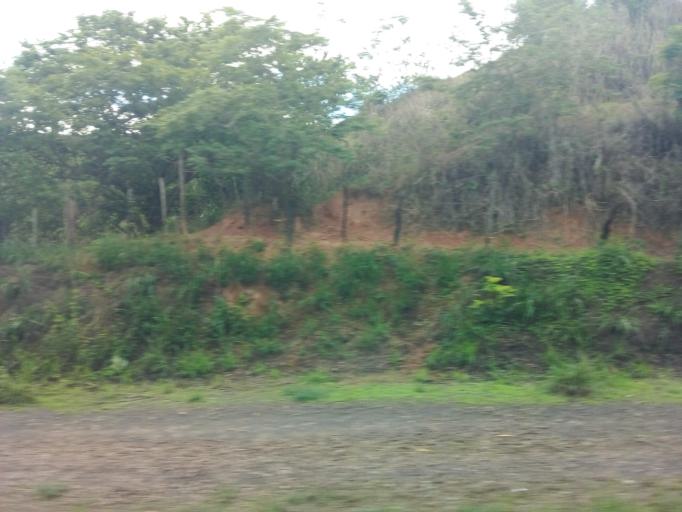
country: BR
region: Minas Gerais
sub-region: Governador Valadares
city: Governador Valadares
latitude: -19.0735
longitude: -42.1538
